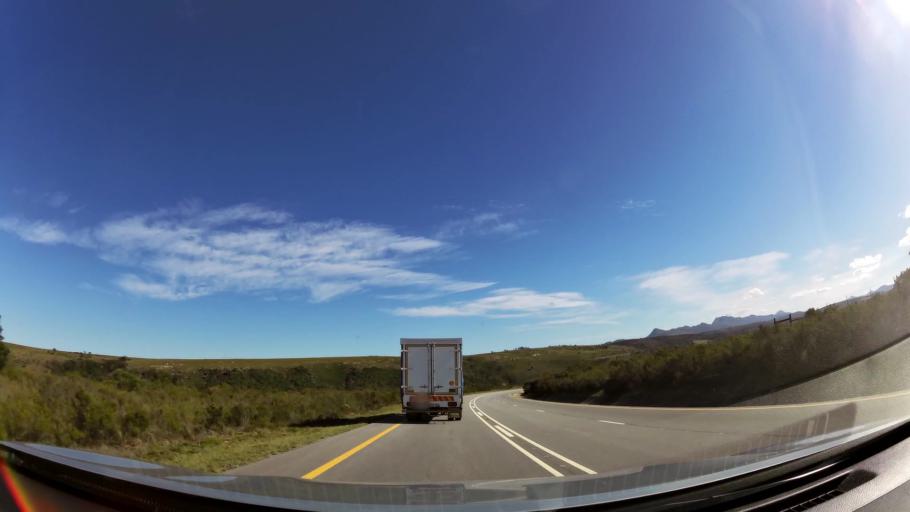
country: ZA
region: Eastern Cape
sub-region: Cacadu District Municipality
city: Kruisfontein
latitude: -34.0407
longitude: 24.5868
